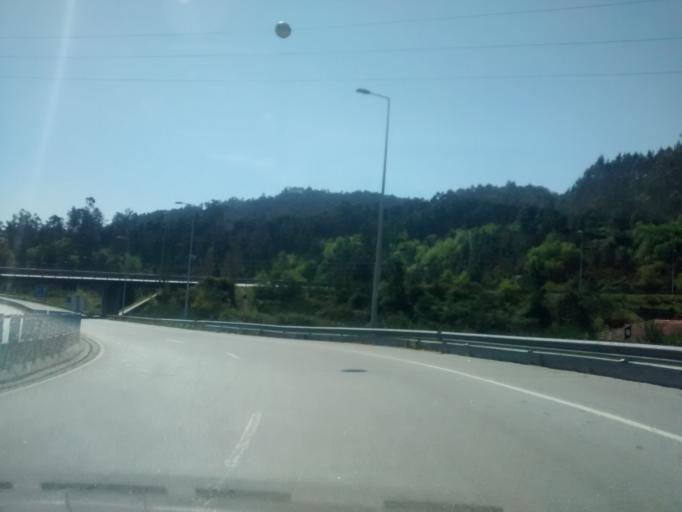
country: PT
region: Braga
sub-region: Braga
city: Oliveira
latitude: 41.5087
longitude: -8.4467
